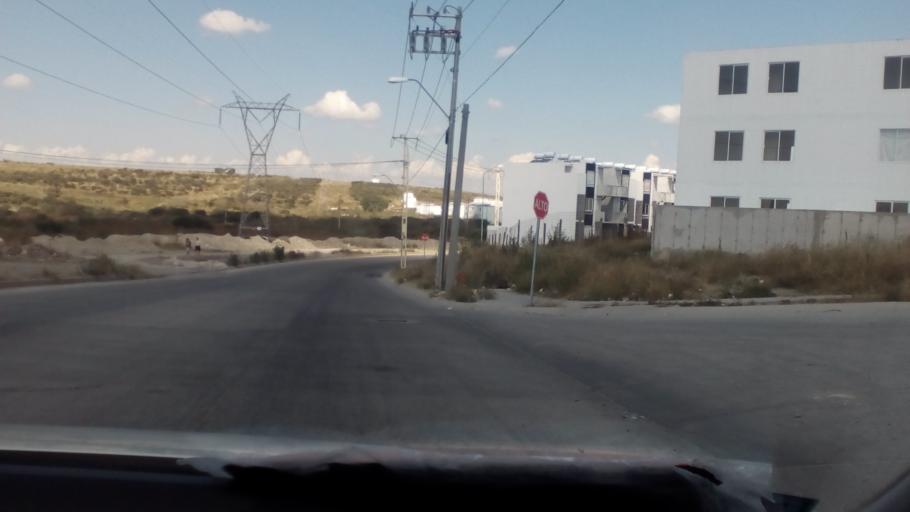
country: MX
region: Guanajuato
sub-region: Leon
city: Fraccionamiento Paseo de las Torres
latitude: 21.1777
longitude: -101.7661
